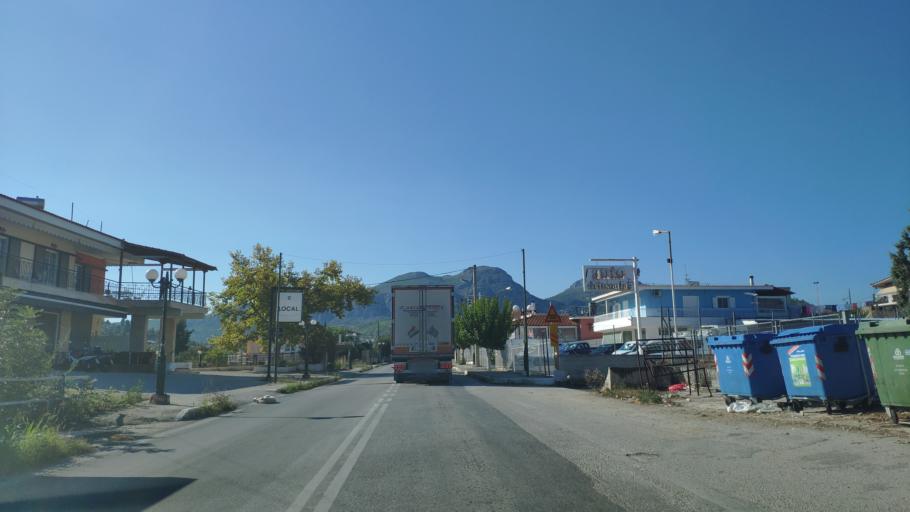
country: GR
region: Peloponnese
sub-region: Nomos Korinthias
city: Arkhaia Korinthos
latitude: 37.8818
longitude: 22.8910
